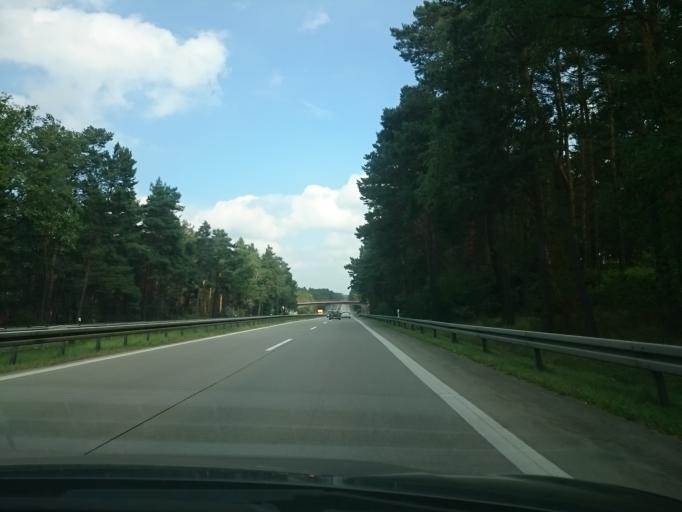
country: DE
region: Brandenburg
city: Marienwerder
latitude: 52.7841
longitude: 13.5809
